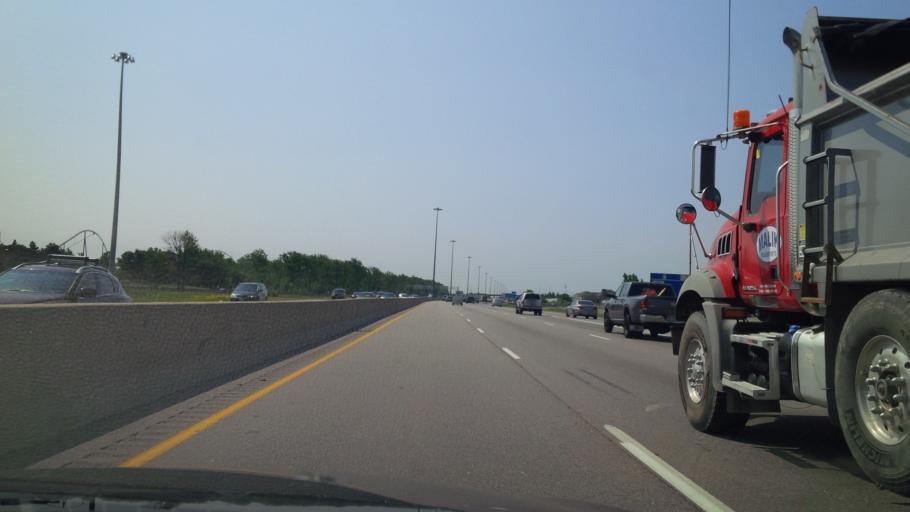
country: CA
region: Ontario
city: Vaughan
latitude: 43.8461
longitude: -79.5485
